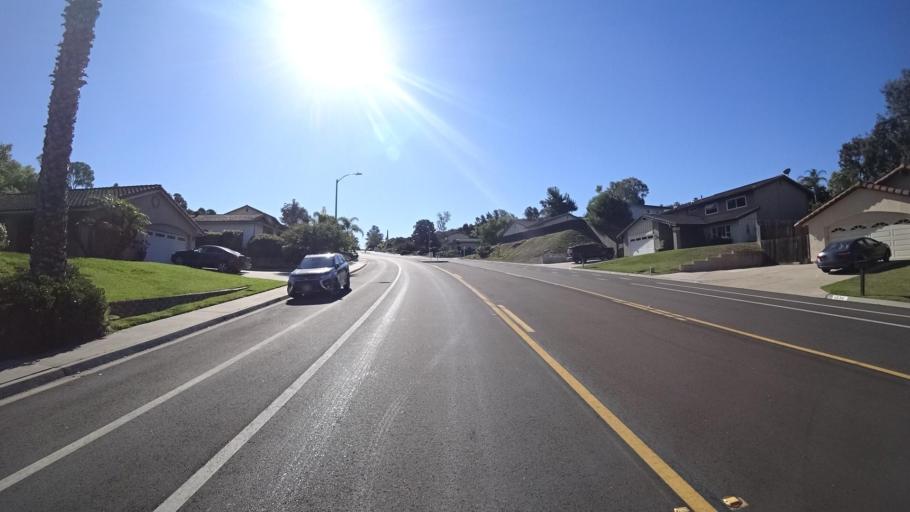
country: US
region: California
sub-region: San Diego County
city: Bonita
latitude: 32.6622
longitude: -117.0006
